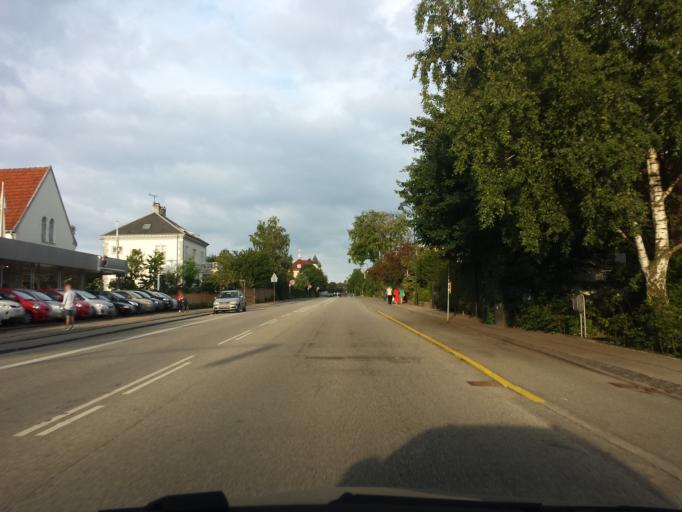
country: DK
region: Capital Region
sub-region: Lyngby-Tarbaek Kommune
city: Kongens Lyngby
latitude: 55.7541
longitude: 12.5346
